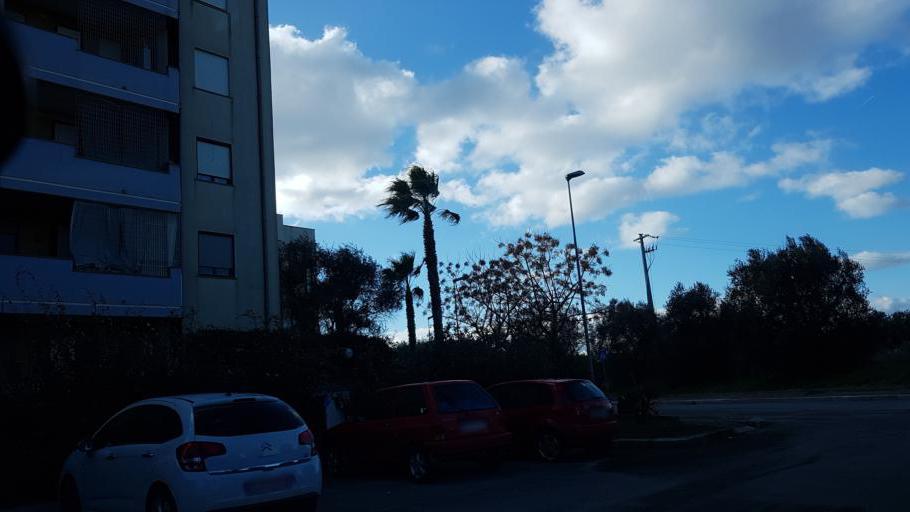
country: IT
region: Apulia
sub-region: Provincia di Brindisi
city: Brindisi
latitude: 40.6512
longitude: 17.9206
